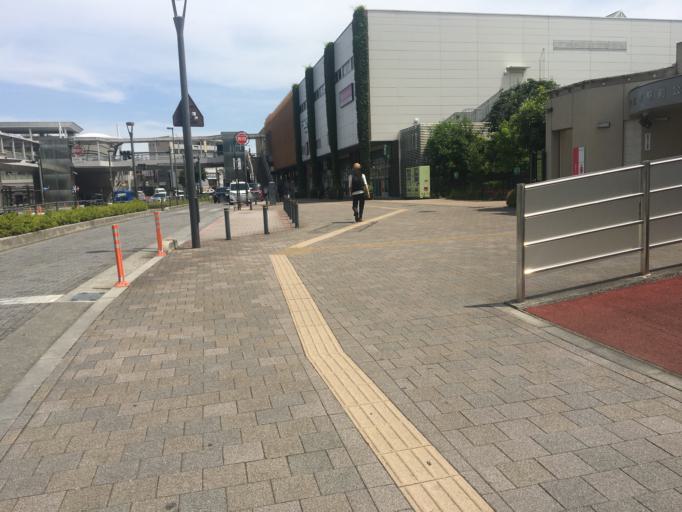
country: JP
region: Saitama
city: Sayama
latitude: 35.8564
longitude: 139.4127
